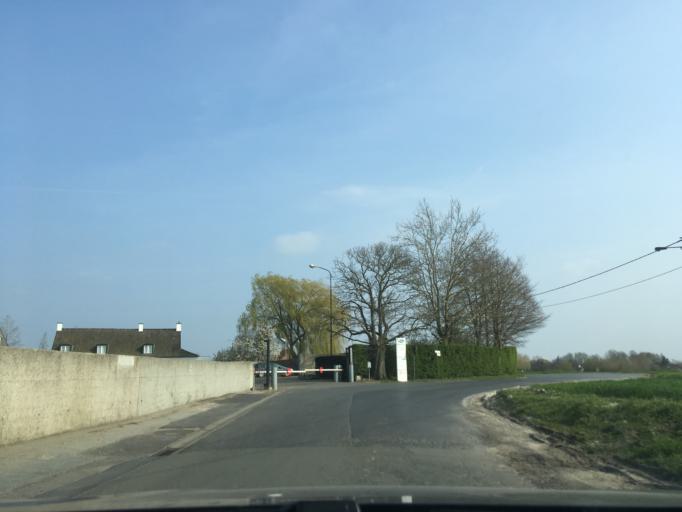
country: BE
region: Flanders
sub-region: Provincie West-Vlaanderen
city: Ardooie
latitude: 50.9531
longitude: 3.2142
